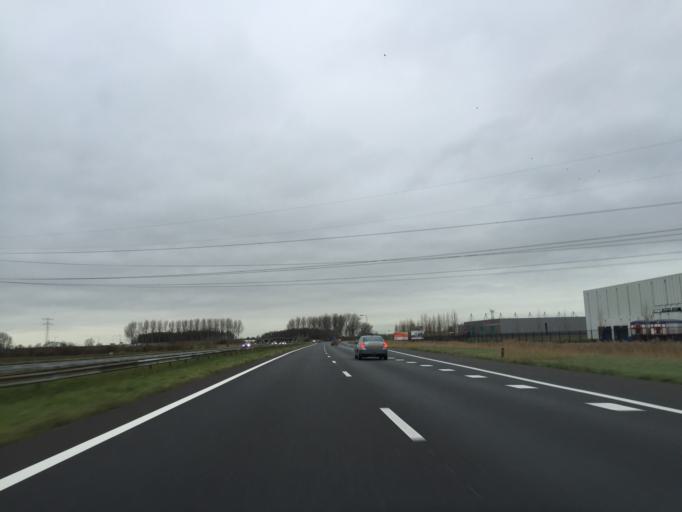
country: NL
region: Zeeland
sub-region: Gemeente Reimerswaal
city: Yerseke
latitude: 51.4581
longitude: 4.0312
